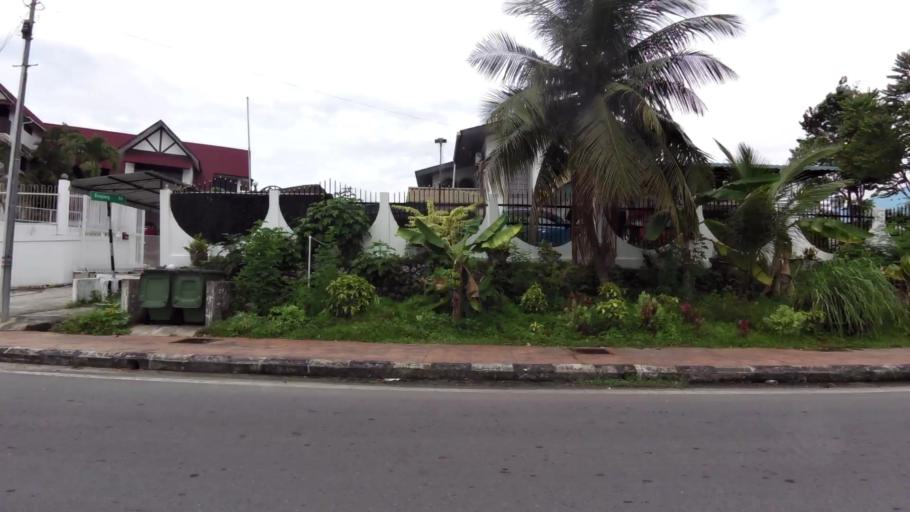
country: BN
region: Brunei and Muara
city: Bandar Seri Begawan
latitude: 4.8957
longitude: 114.9282
